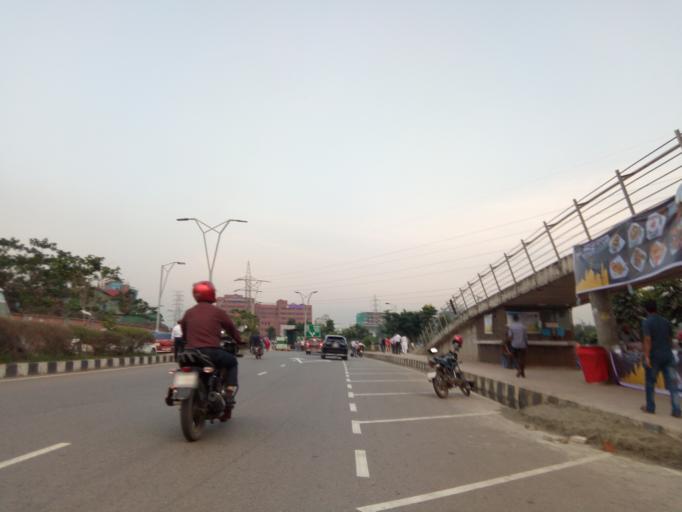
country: BD
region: Dhaka
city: Paltan
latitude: 23.7708
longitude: 90.4224
